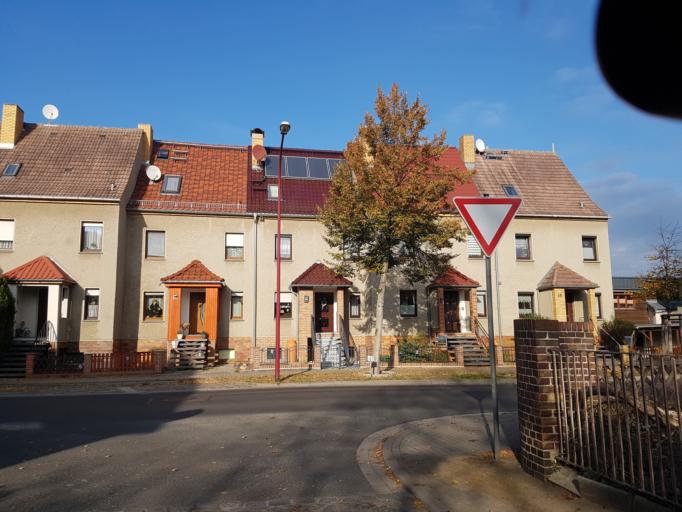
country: DE
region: Brandenburg
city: Finsterwalde
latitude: 51.6240
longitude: 13.7196
